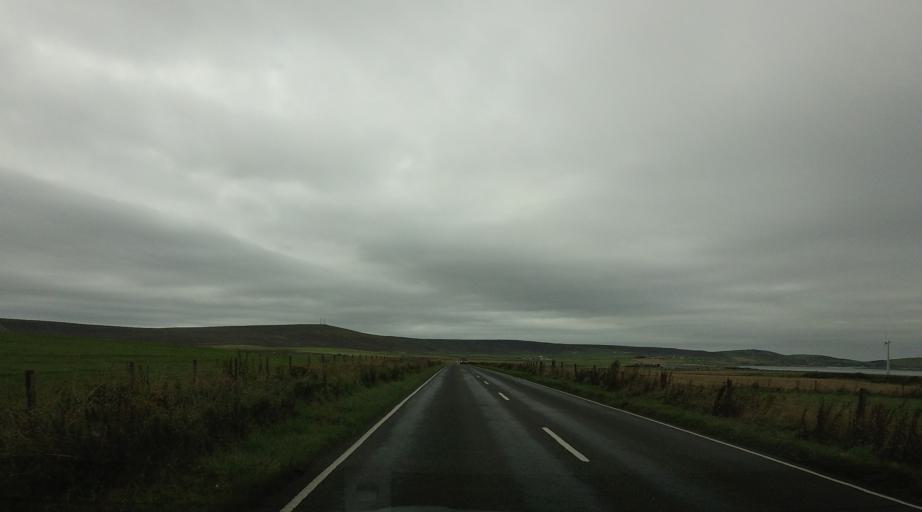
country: GB
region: Scotland
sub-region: Orkney Islands
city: Orkney
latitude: 58.9969
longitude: -3.0363
